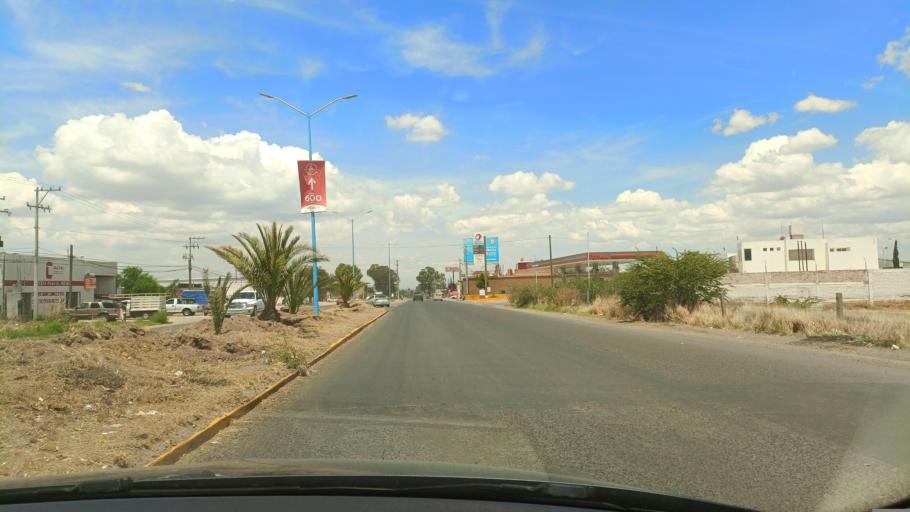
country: MX
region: Guanajuato
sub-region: San Luis de la Paz
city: San Ignacio
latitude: 21.2942
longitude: -100.5347
